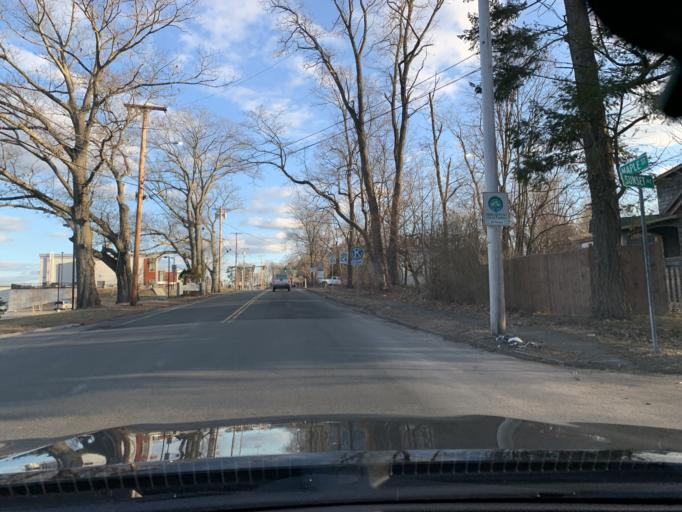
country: US
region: Massachusetts
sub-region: Essex County
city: Middleton
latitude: 42.5930
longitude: -70.9817
